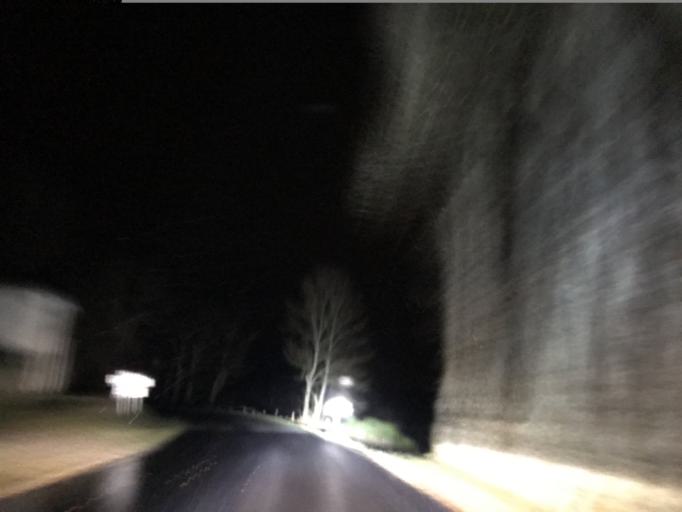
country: FR
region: Auvergne
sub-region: Departement du Puy-de-Dome
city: Saint-Remy-sur-Durolle
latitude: 45.9038
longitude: 3.6292
